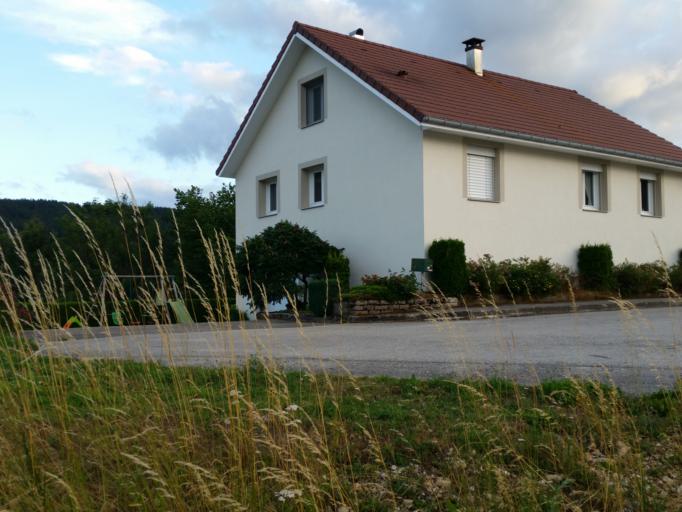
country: CH
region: Vaud
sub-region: Jura-Nord vaudois District
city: Vallorbe
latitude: 46.7466
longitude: 6.2915
